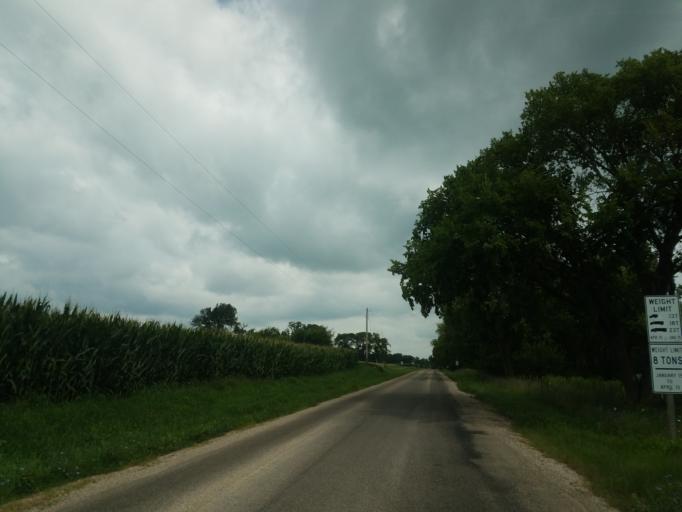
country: US
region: Illinois
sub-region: McLean County
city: Twin Grove
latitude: 40.4588
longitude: -89.0455
